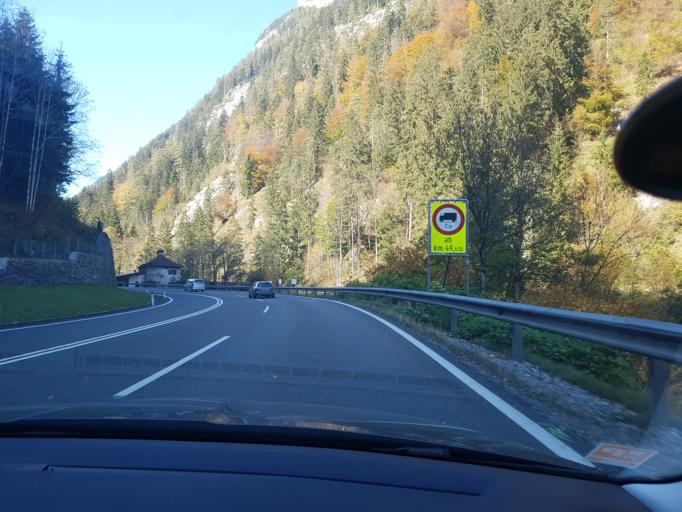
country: AT
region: Salzburg
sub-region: Politischer Bezirk Zell am See
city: Lofer
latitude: 47.5789
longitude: 12.6658
